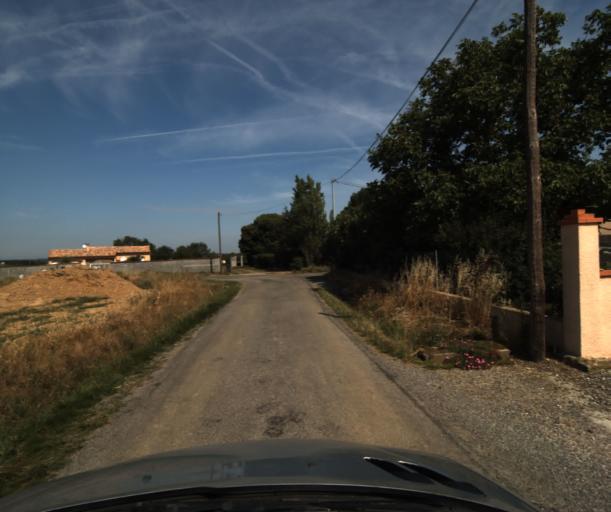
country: FR
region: Midi-Pyrenees
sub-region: Departement de la Haute-Garonne
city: Lherm
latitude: 43.4546
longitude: 1.1850
